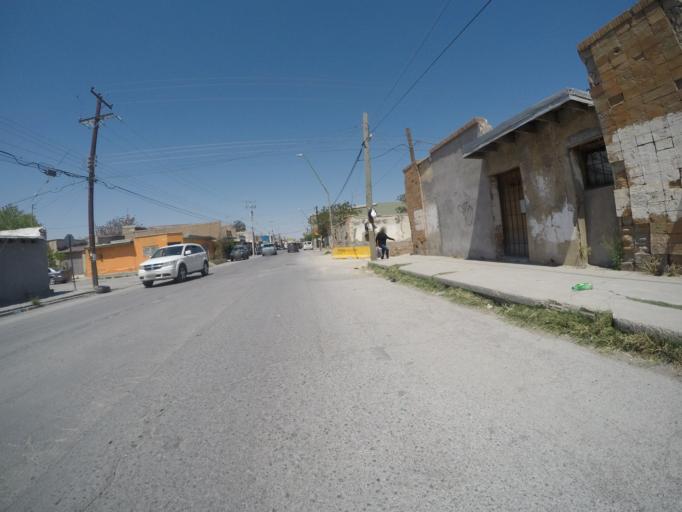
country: MX
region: Chihuahua
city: Ciudad Juarez
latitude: 31.7321
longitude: -106.4822
